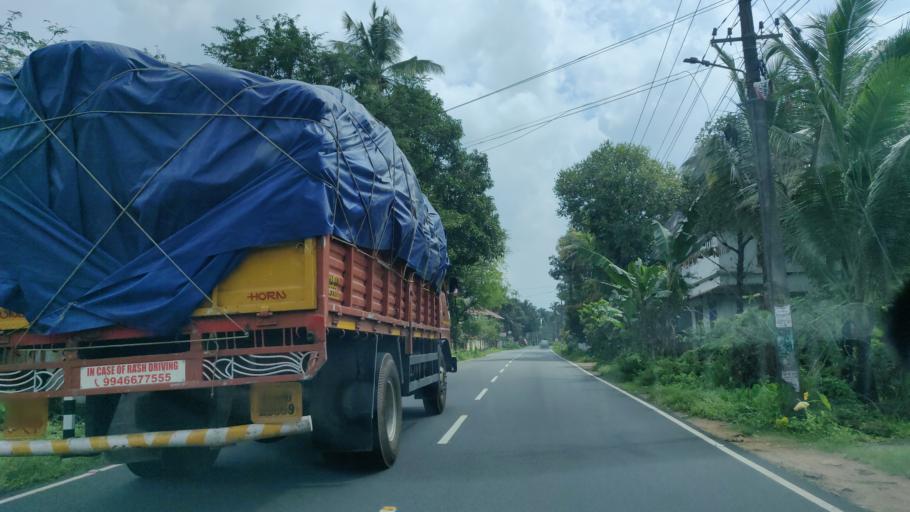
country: IN
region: Kerala
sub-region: Ernakulam
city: Angamali
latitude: 10.1663
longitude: 76.4132
